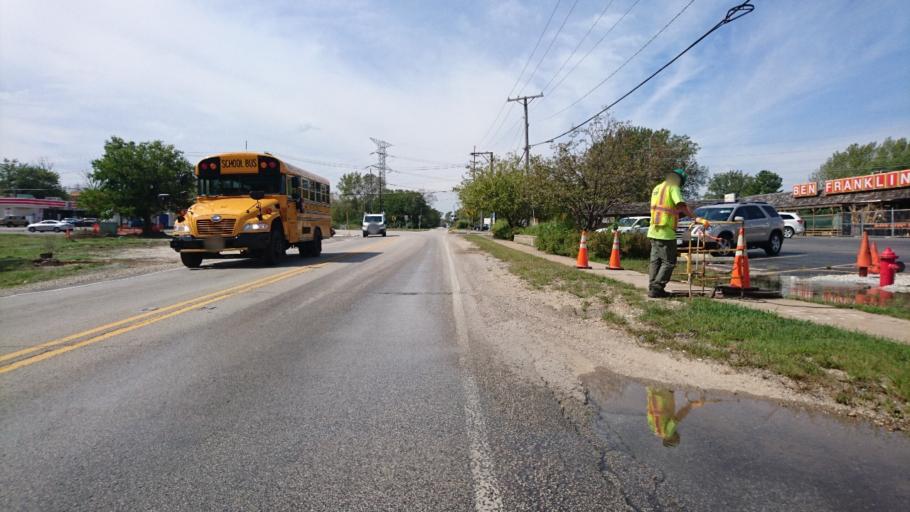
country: US
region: Illinois
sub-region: Will County
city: Wilmington
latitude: 41.3052
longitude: -88.1581
